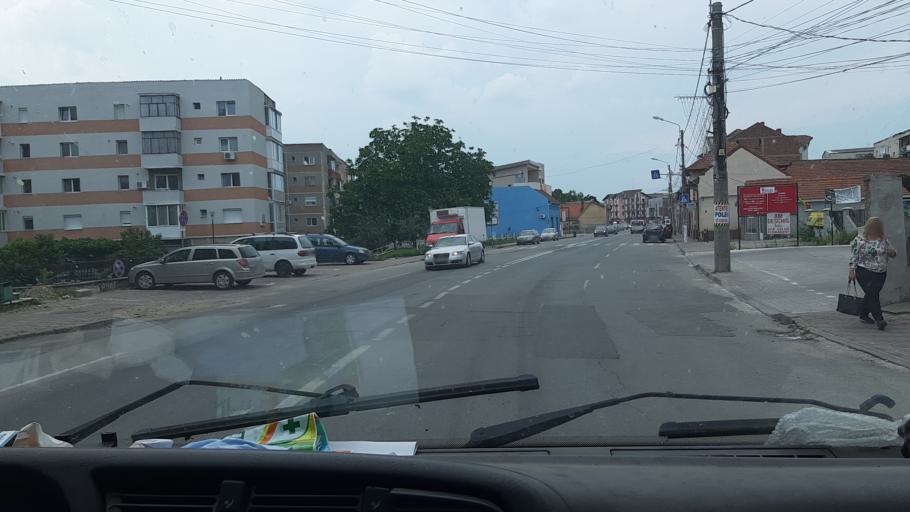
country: RO
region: Timis
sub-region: Municipiul Lugoj
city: Lugoj
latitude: 45.6922
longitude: 21.9022
